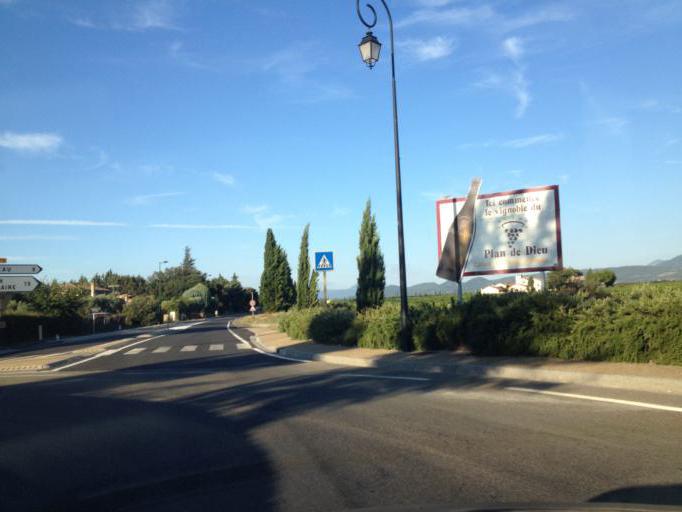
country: FR
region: Provence-Alpes-Cote d'Azur
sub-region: Departement du Vaucluse
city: Camaret-sur-Aigues
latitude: 44.1827
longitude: 4.9029
